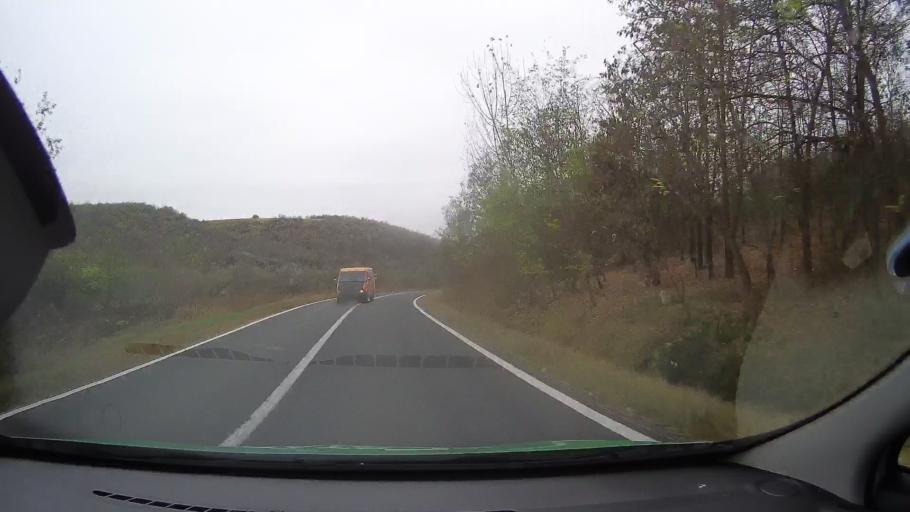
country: RO
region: Constanta
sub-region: Comuna Garliciu
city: Garliciu
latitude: 44.7065
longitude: 28.0701
